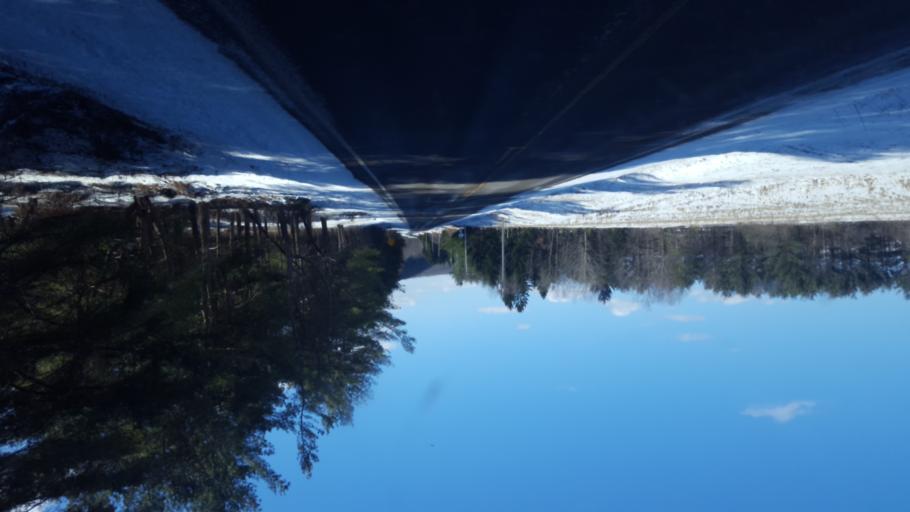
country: US
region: New York
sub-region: Allegany County
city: Belmont
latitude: 42.1791
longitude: -78.0738
